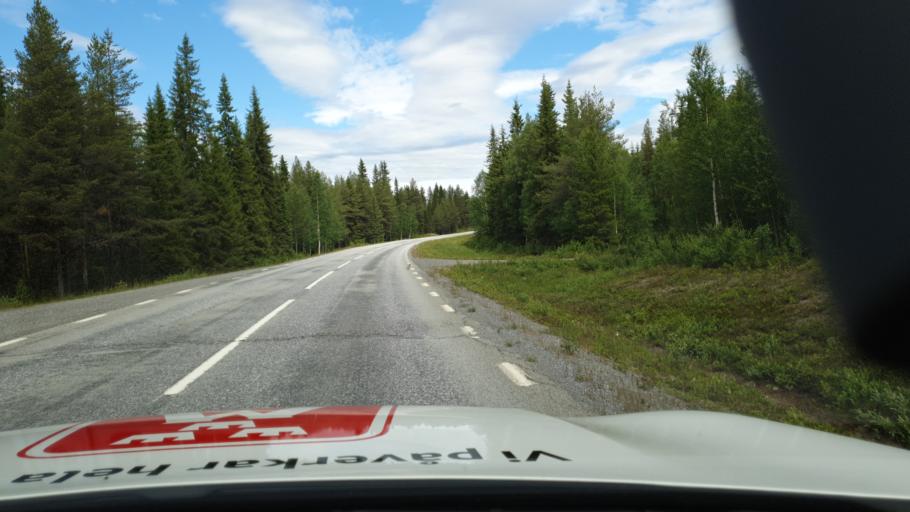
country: SE
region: Vaesterbotten
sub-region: Storumans Kommun
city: Fristad
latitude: 65.3674
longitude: 16.5212
